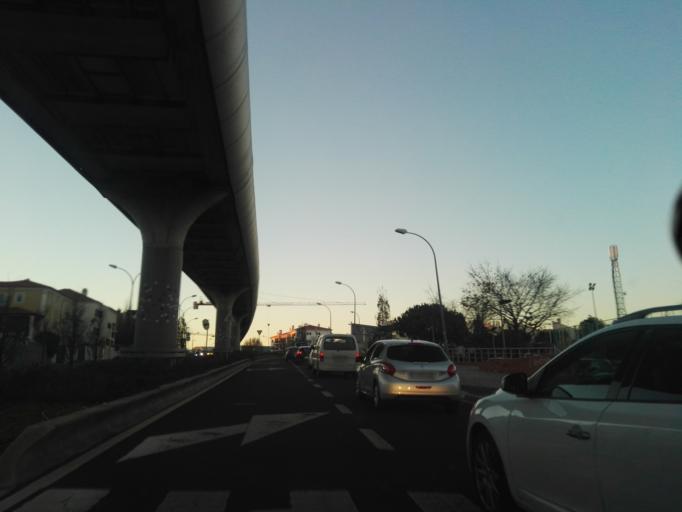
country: PT
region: Lisbon
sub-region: Oeiras
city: Paco de Arcos
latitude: 38.7024
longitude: -9.2987
